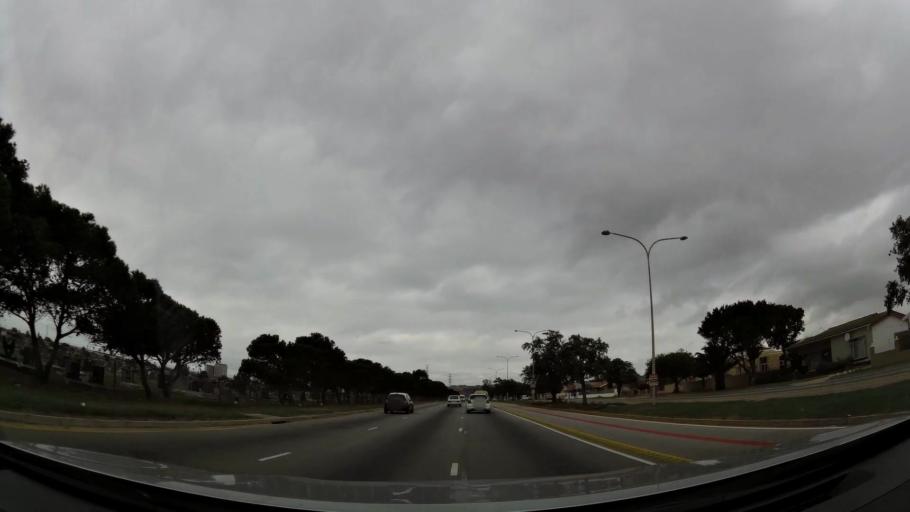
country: ZA
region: Eastern Cape
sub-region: Nelson Mandela Bay Metropolitan Municipality
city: Port Elizabeth
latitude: -33.9166
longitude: 25.5636
